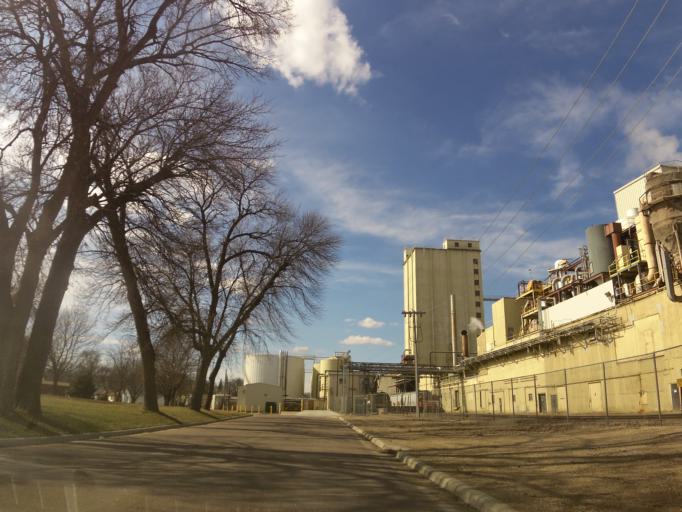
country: US
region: Minnesota
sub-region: Lac qui Parle County
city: Dawson
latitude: 44.9315
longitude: -96.0567
